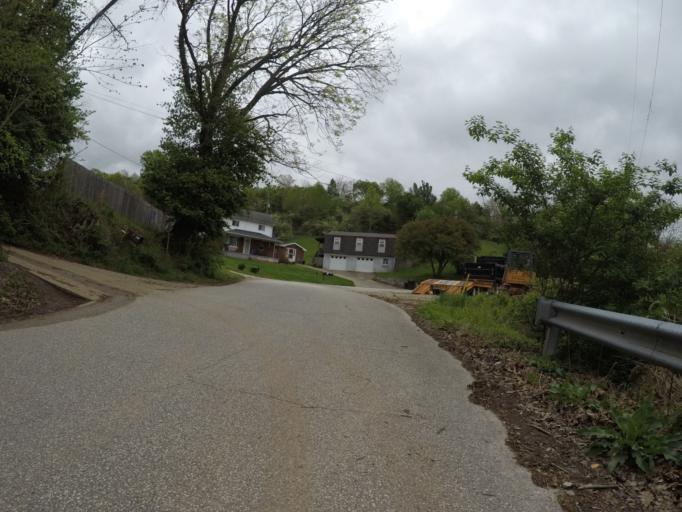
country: US
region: West Virginia
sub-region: Cabell County
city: Barboursville
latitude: 38.4021
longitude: -82.2735
